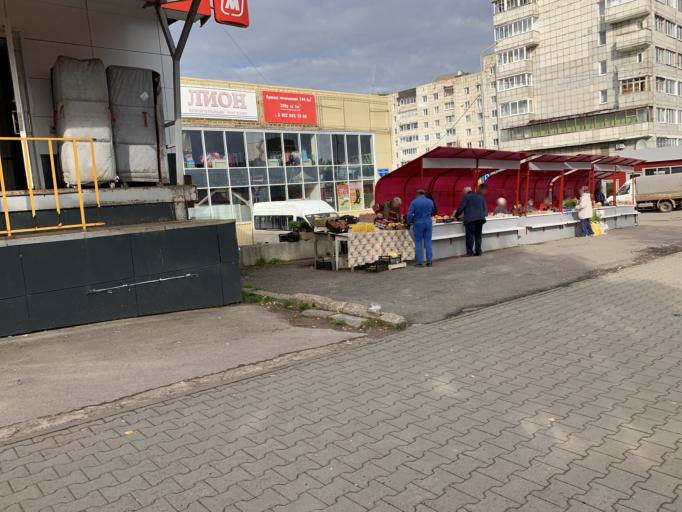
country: RU
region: Perm
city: Gubakha
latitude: 58.8353
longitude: 57.5553
